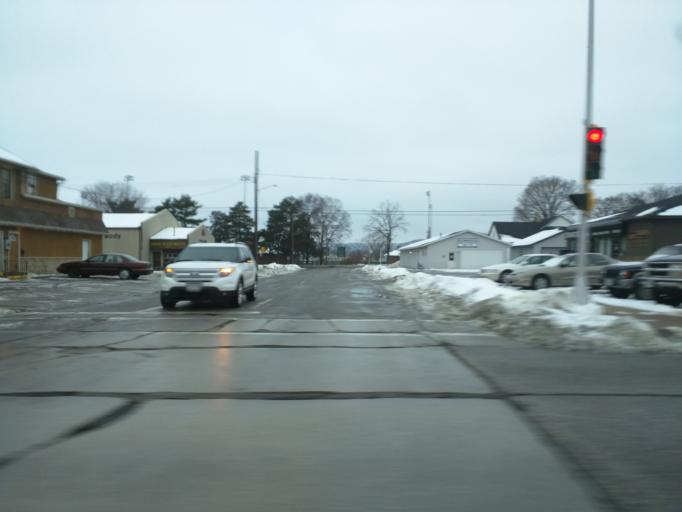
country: US
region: Wisconsin
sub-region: La Crosse County
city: North La Crosse
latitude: 43.8369
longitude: -91.2482
